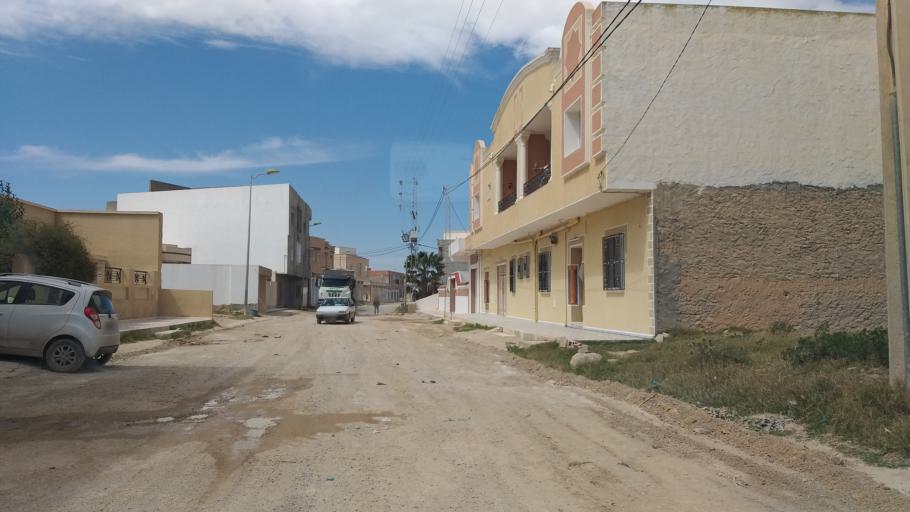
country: TN
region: Al Mahdiyah
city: El Jem
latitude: 35.3033
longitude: 10.6960
